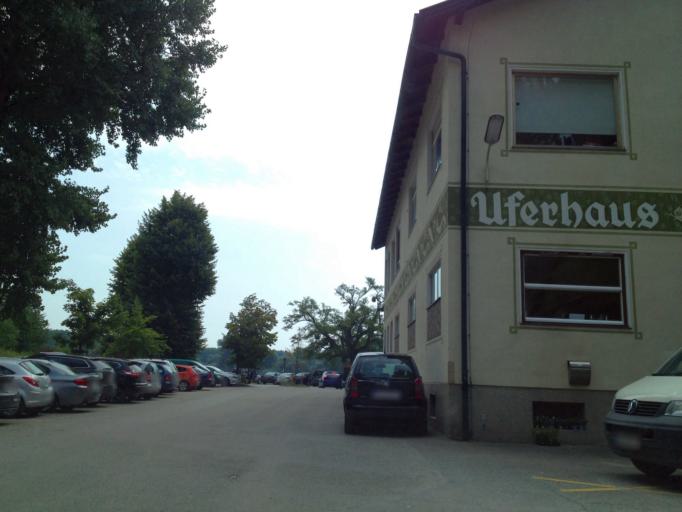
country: AT
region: Lower Austria
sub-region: Politischer Bezirk Ganserndorf
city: Orth an der Donau
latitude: 48.1248
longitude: 16.7120
